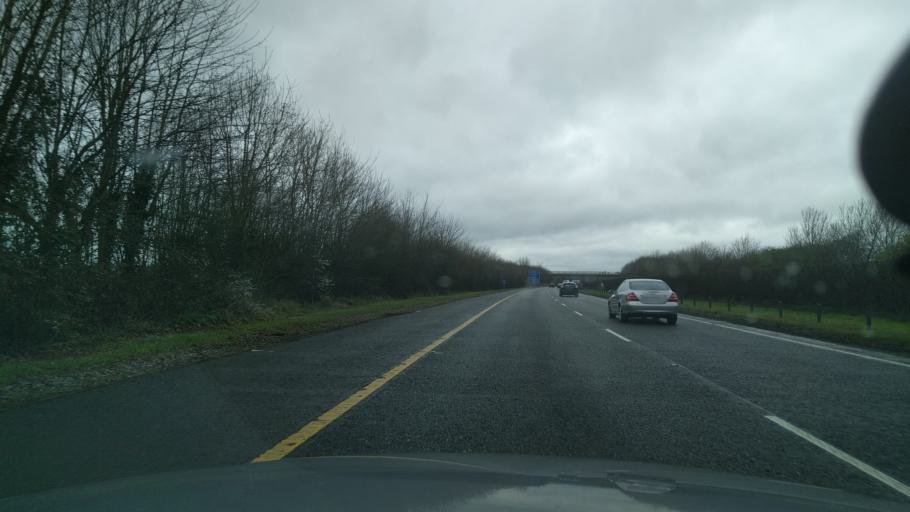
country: IE
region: Leinster
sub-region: Kildare
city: Kilcock
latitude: 53.3825
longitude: -6.6586
